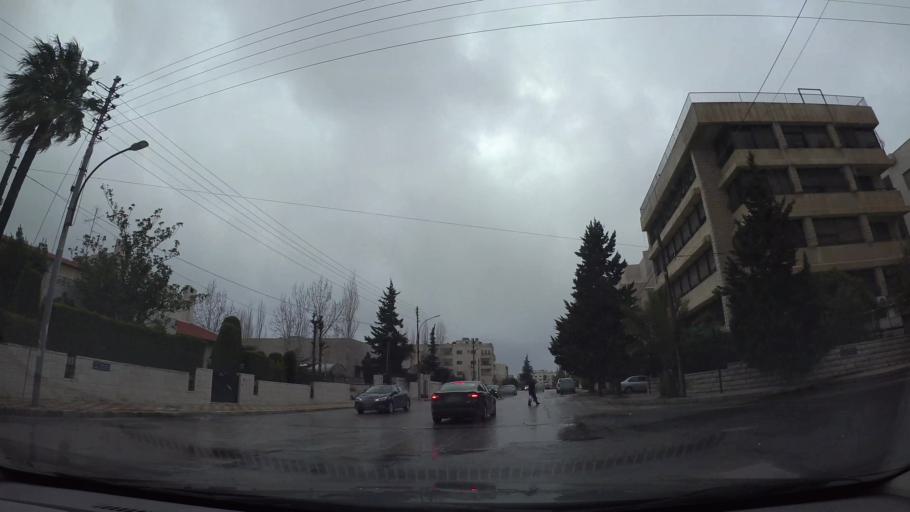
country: JO
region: Amman
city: Wadi as Sir
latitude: 31.9543
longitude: 35.8740
